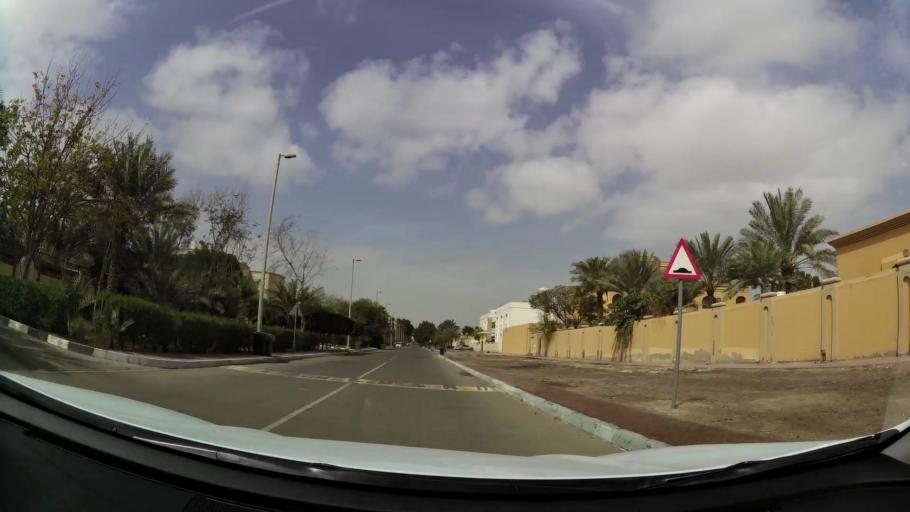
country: AE
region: Abu Dhabi
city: Abu Dhabi
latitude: 24.4031
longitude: 54.5209
